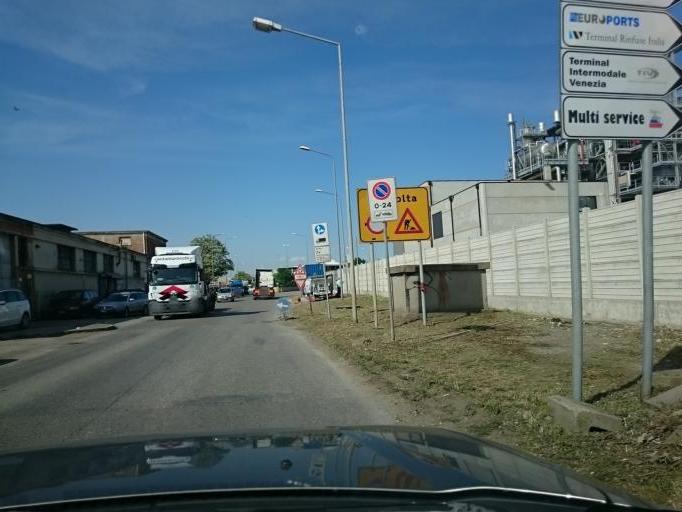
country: IT
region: Veneto
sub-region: Provincia di Venezia
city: Mestre
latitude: 45.4710
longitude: 12.2319
